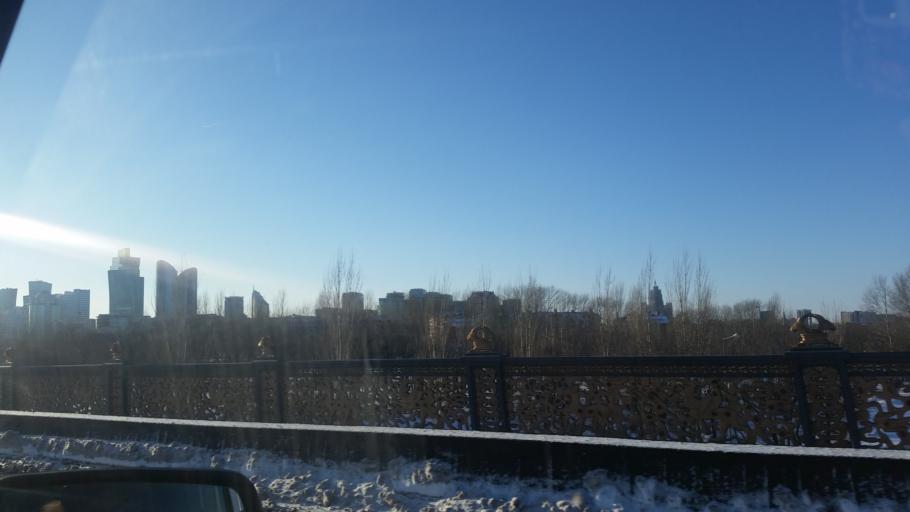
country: KZ
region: Astana Qalasy
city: Astana
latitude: 51.1373
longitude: 71.4428
